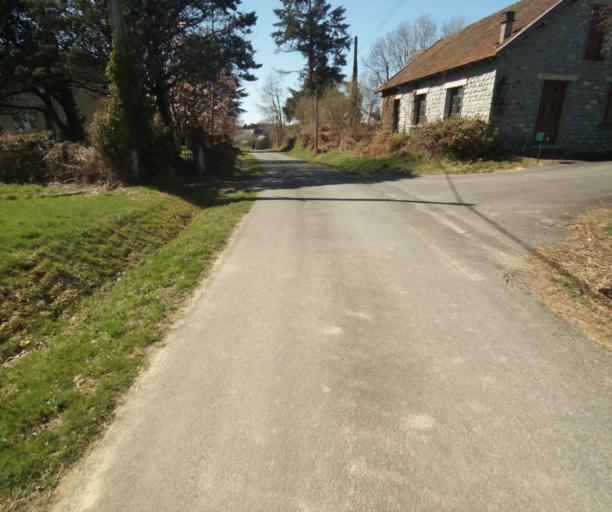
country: FR
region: Limousin
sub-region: Departement de la Correze
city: Saint-Mexant
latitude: 45.2972
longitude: 1.6675
